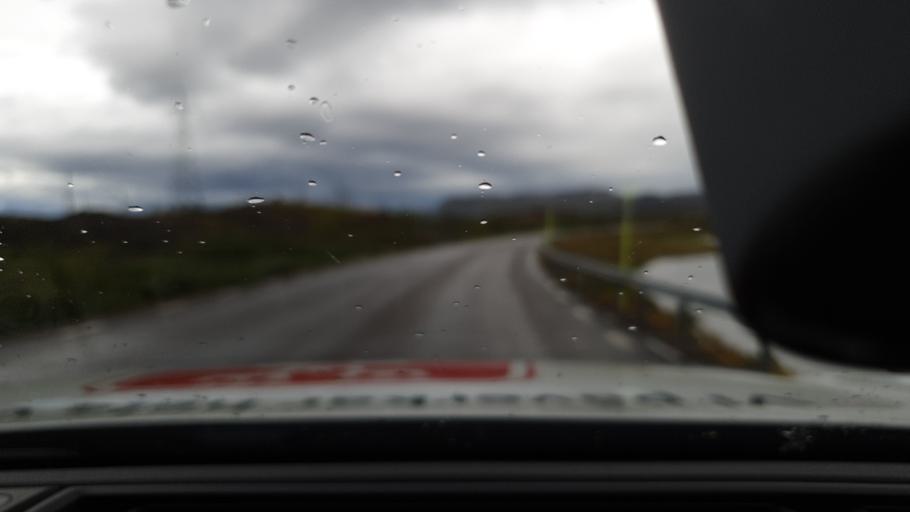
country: NO
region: Troms
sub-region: Bardu
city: Setermoen
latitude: 68.4281
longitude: 18.2724
